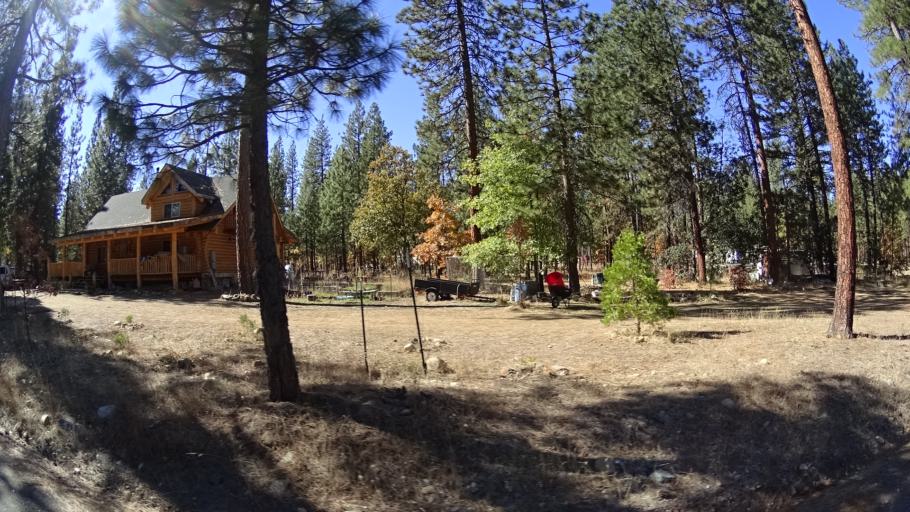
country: US
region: California
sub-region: Siskiyou County
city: Yreka
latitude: 41.5988
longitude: -122.9742
